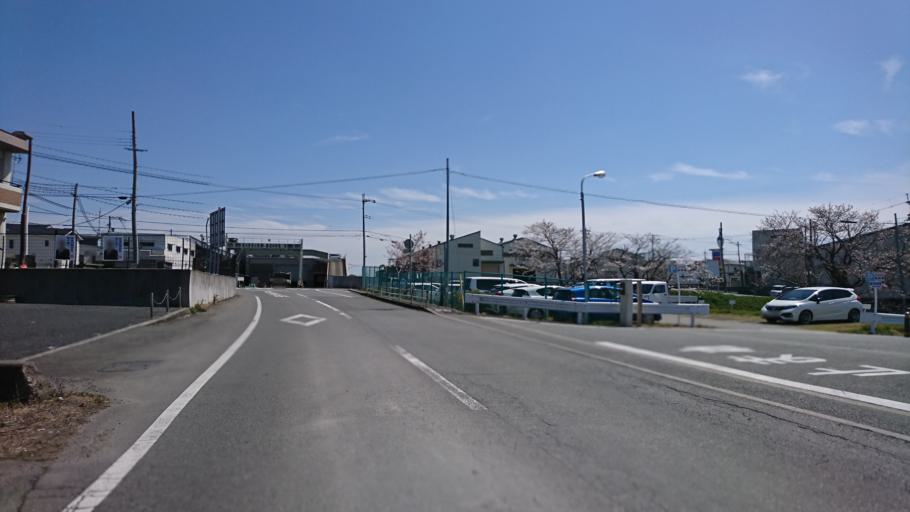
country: JP
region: Hyogo
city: Kakogawacho-honmachi
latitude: 34.7301
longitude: 134.9024
